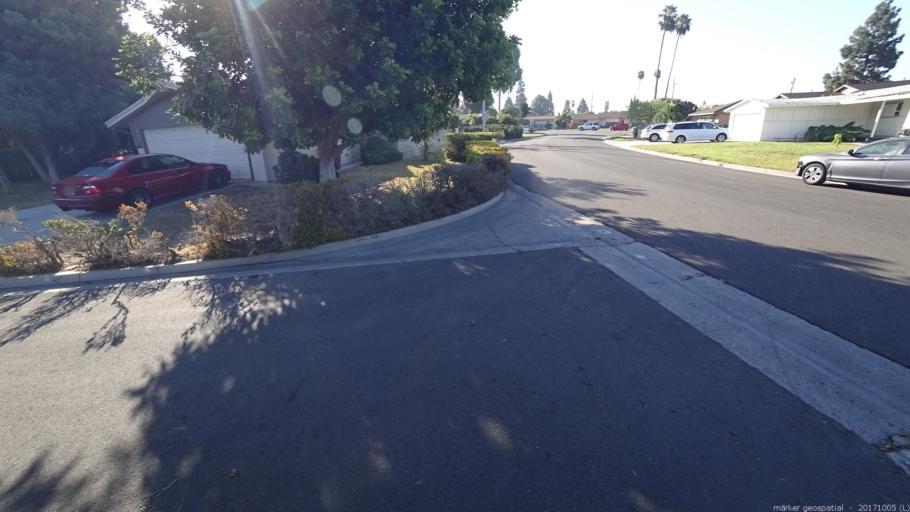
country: US
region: California
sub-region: Orange County
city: Garden Grove
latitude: 33.7971
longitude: -117.9507
